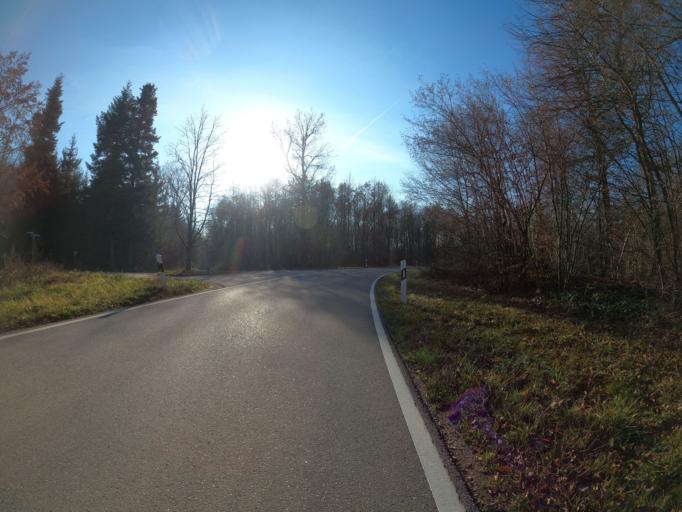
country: DE
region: Baden-Wuerttemberg
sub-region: Regierungsbezirk Stuttgart
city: Albershausen
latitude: 48.6927
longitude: 9.5382
